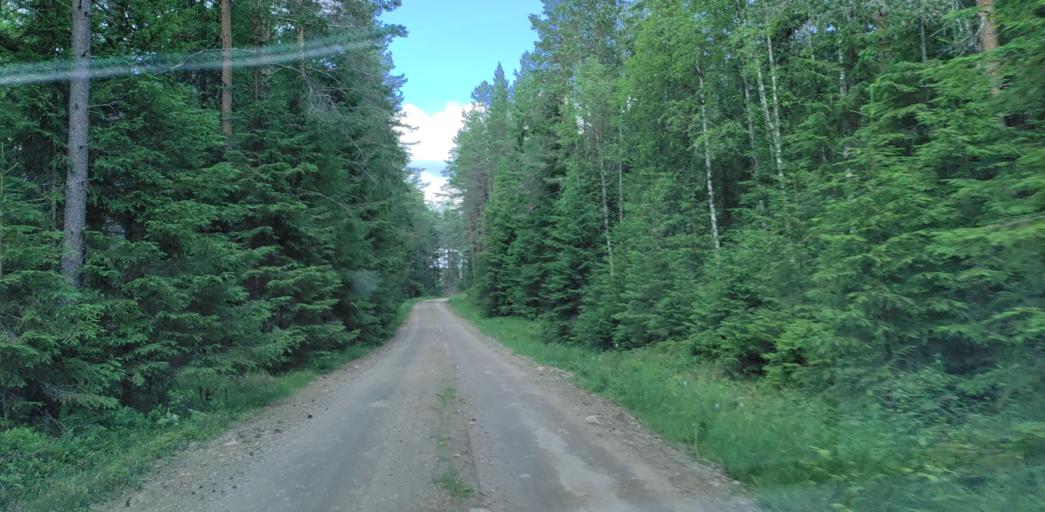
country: SE
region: Vaermland
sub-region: Hagfors Kommun
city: Ekshaerad
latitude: 60.0825
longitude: 13.3454
